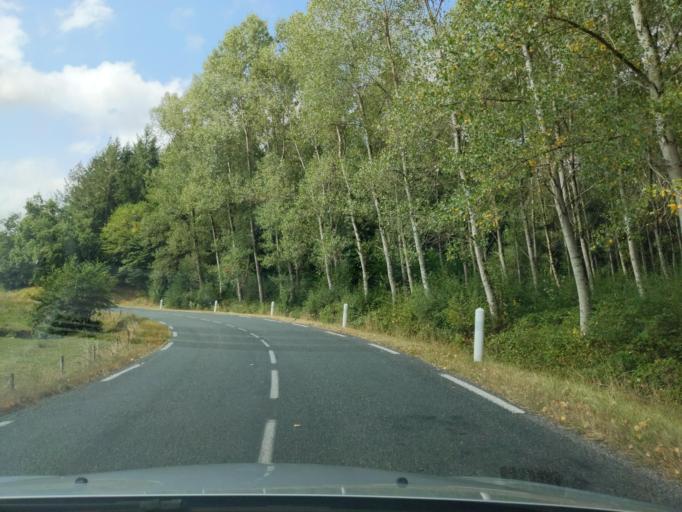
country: FR
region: Bourgogne
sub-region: Departement de la Nievre
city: Luzy
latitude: 46.7129
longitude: 3.8789
